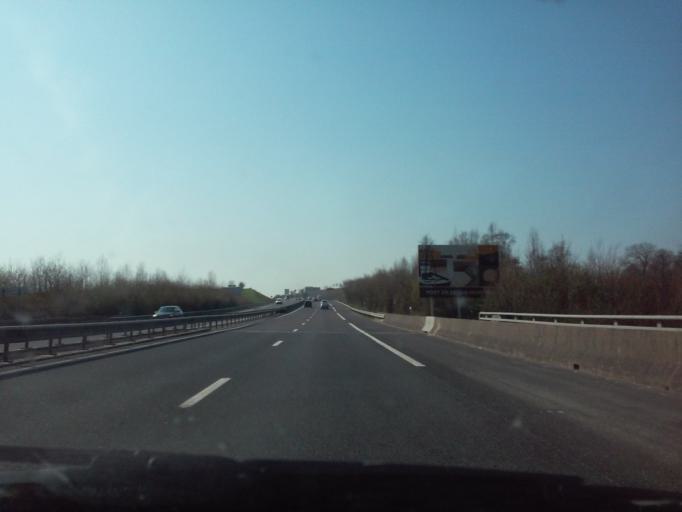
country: FR
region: Lower Normandy
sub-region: Departement du Calvados
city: Saint-Vigor-le-Grand
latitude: 49.2506
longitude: -0.6352
